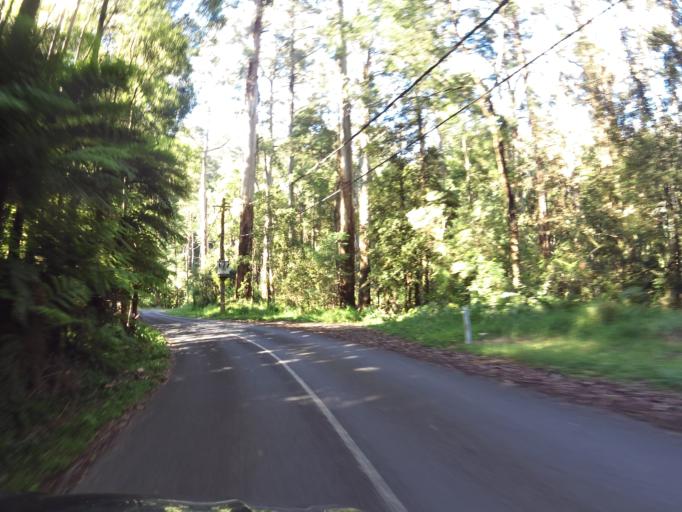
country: AU
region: Victoria
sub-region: Yarra Ranges
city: Kallista
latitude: -37.8667
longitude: 145.3560
